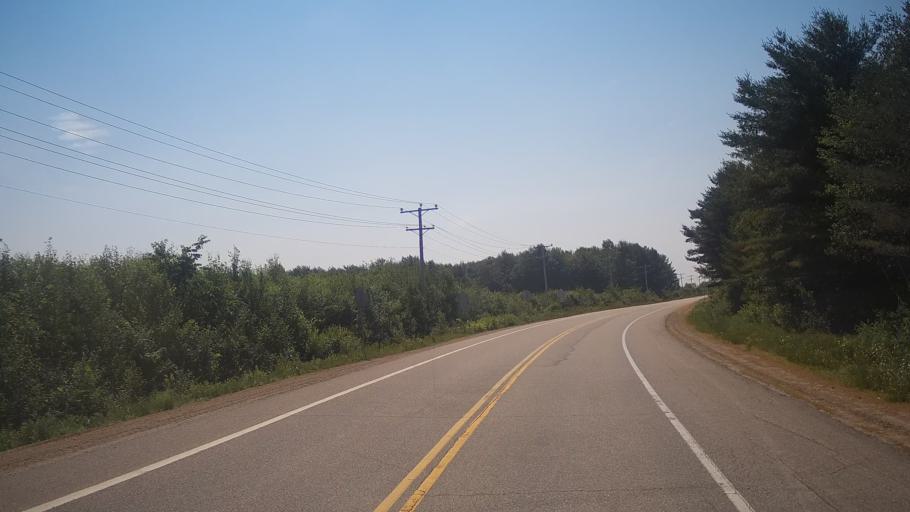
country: CA
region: Ontario
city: Pembroke
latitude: 45.8809
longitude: -76.9516
